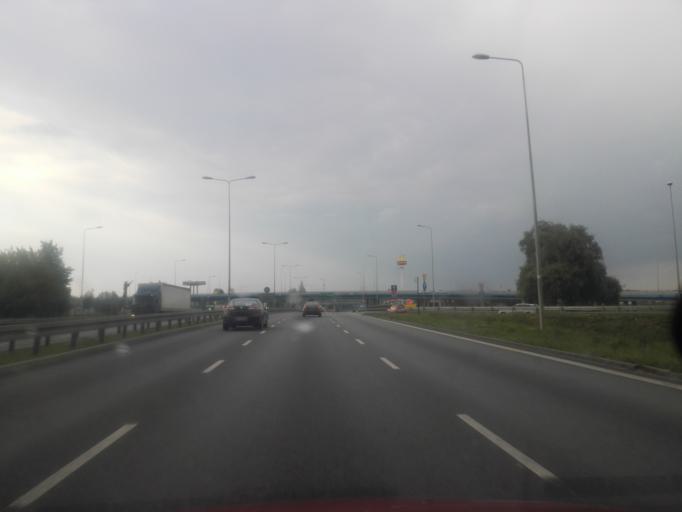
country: PL
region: Silesian Voivodeship
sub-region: Czestochowa
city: Czestochowa
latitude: 50.8164
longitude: 19.1381
